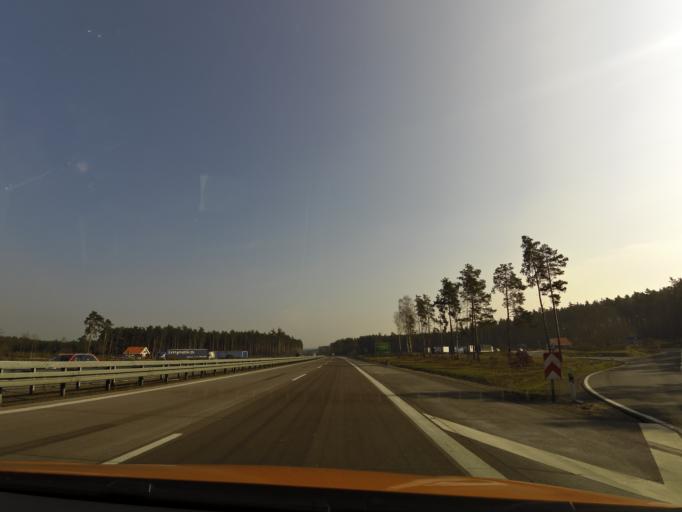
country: DE
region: Brandenburg
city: Storkow
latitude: 52.3115
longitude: 13.9499
